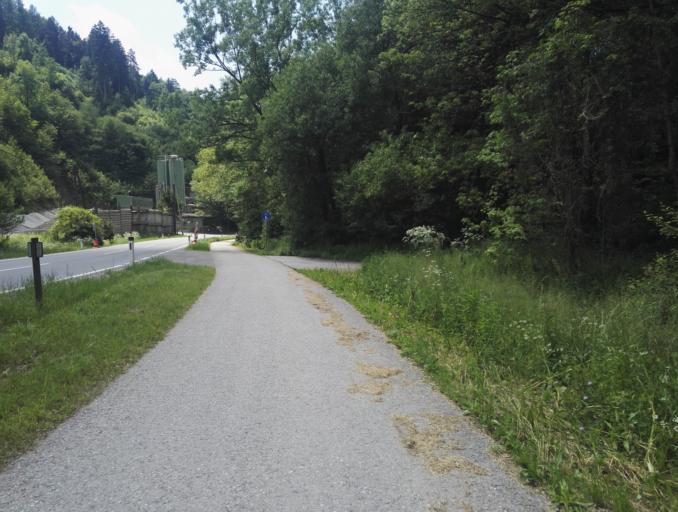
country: AT
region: Styria
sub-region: Politischer Bezirk Graz-Umgebung
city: Stattegg
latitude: 47.1338
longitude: 15.4554
